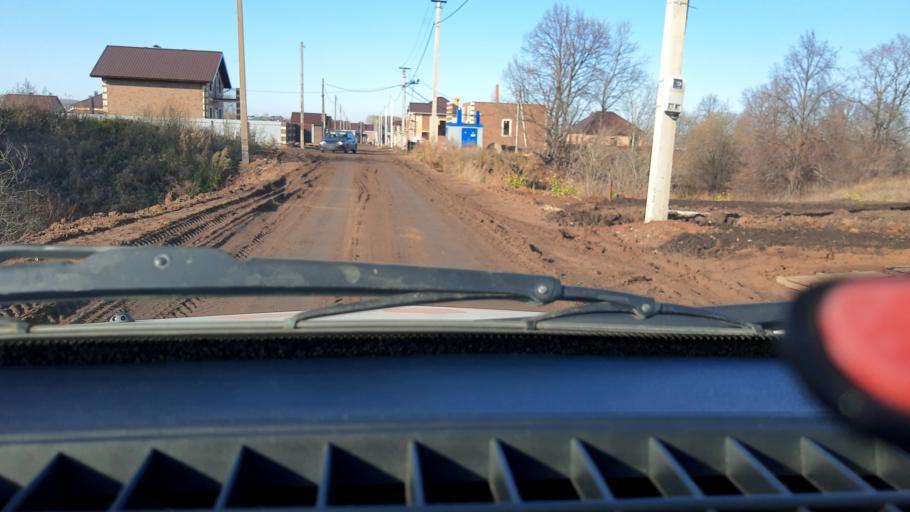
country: RU
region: Bashkortostan
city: Kabakovo
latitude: 54.6271
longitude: 56.1302
